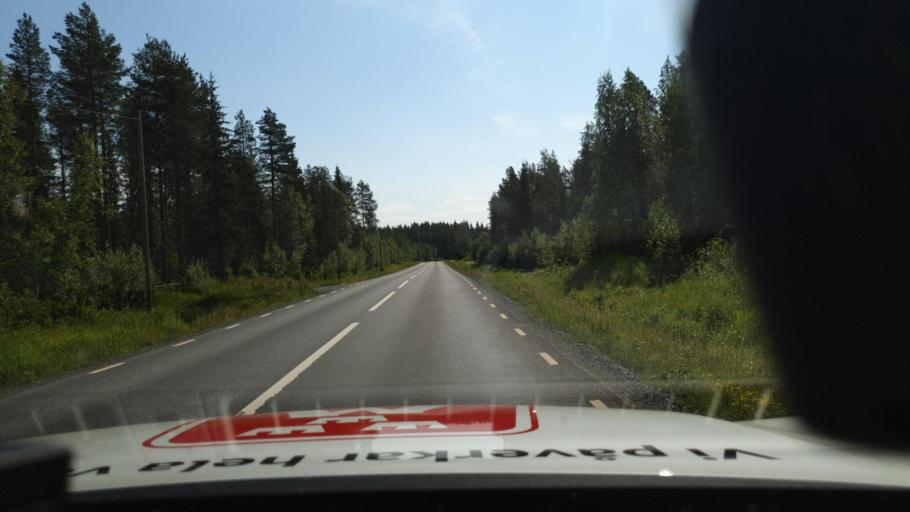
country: SE
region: Norrbotten
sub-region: Lulea Kommun
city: Ranea
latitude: 65.7898
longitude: 22.1453
